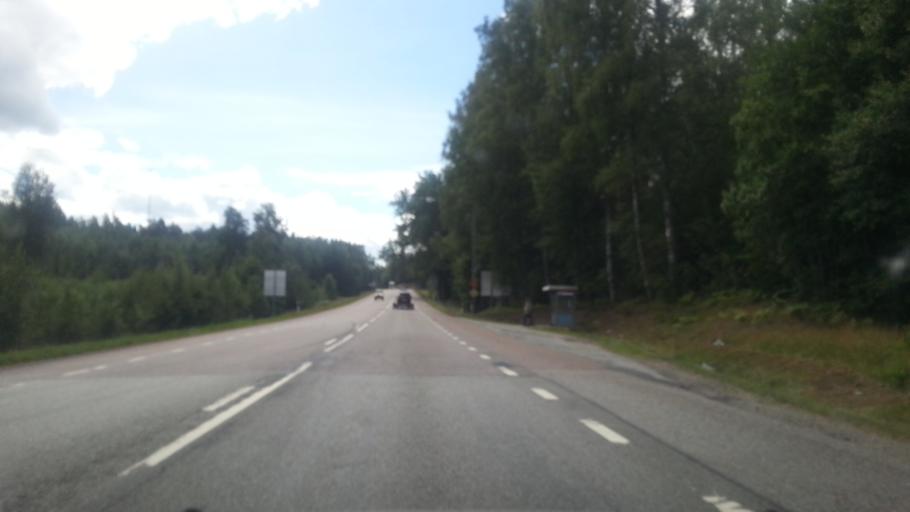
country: SE
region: OErebro
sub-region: Nora Kommun
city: Nora
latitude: 59.4649
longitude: 15.1315
